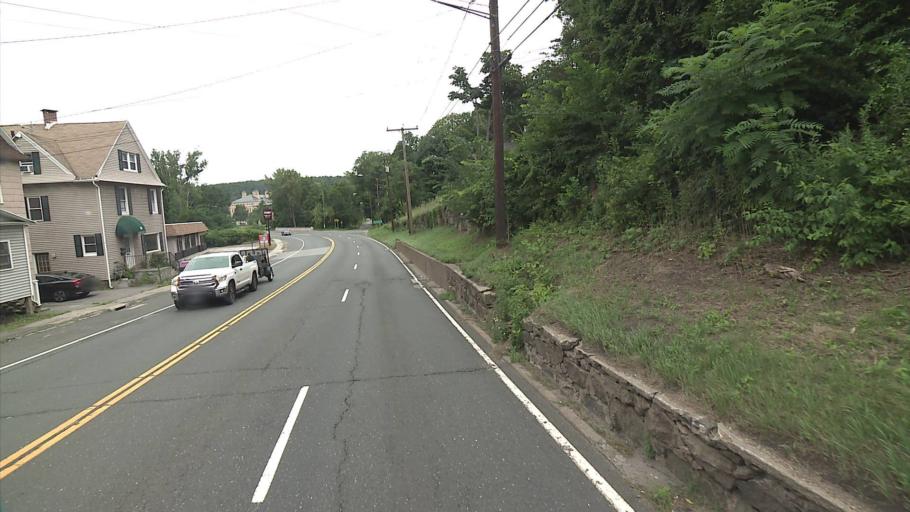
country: US
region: Connecticut
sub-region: Litchfield County
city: Winsted
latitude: 41.9183
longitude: -73.0569
